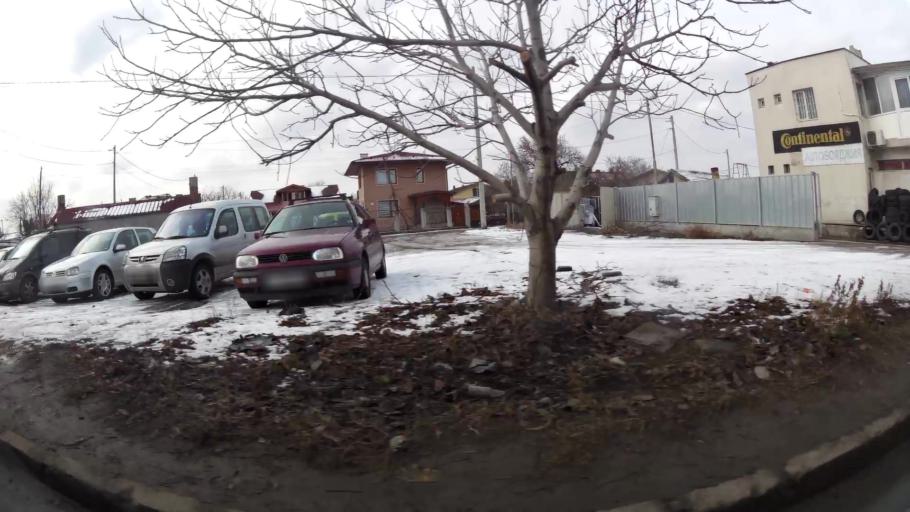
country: BG
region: Sofia-Capital
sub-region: Stolichna Obshtina
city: Sofia
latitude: 42.6968
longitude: 23.3838
